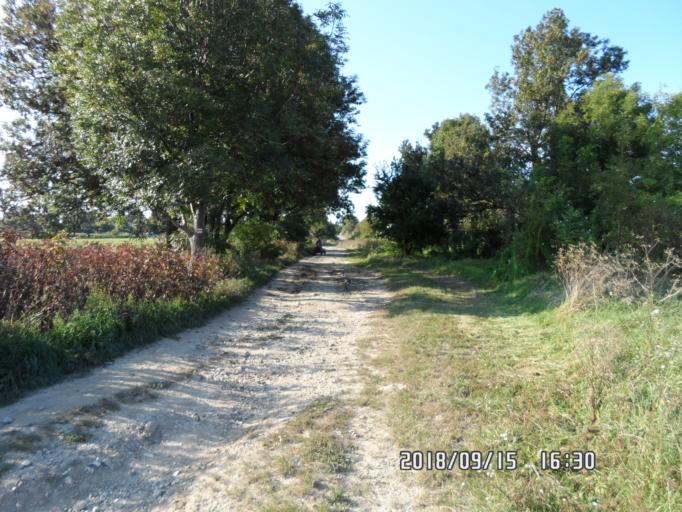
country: HU
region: Veszprem
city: Cseteny
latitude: 47.2525
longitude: 18.0300
